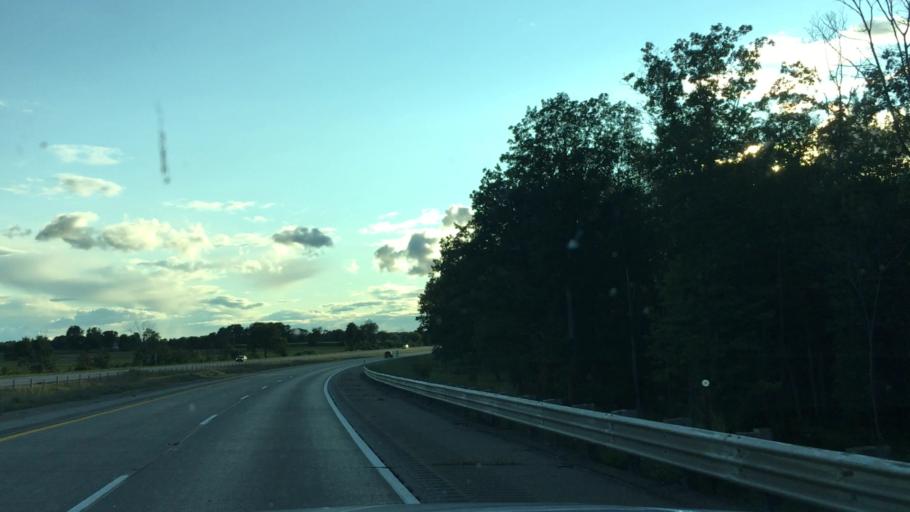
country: US
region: Michigan
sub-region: Kent County
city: Lowell
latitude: 42.8761
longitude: -85.3148
